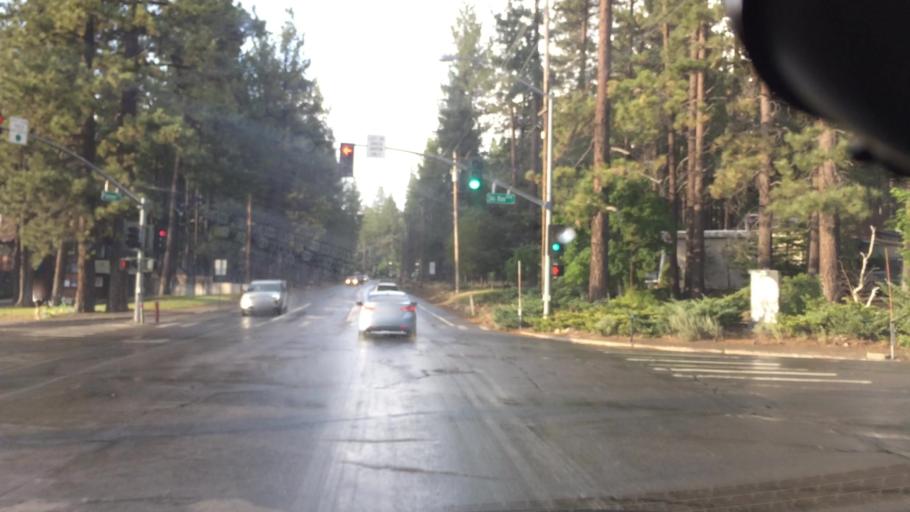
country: US
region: California
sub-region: El Dorado County
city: South Lake Tahoe
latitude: 38.9411
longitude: -119.9523
